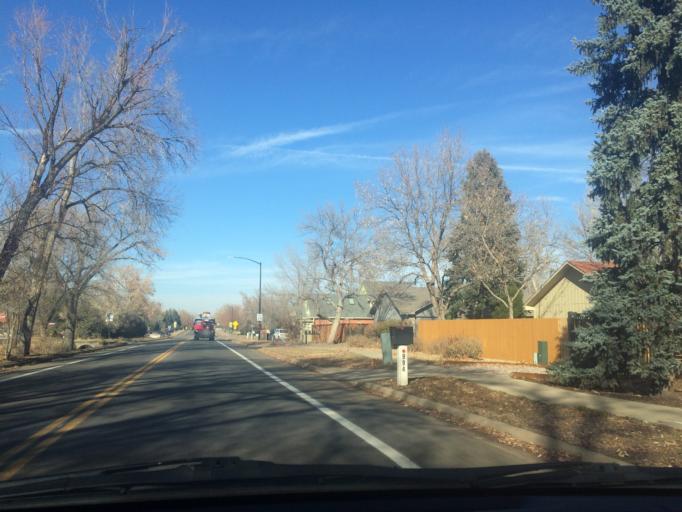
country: US
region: Colorado
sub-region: Boulder County
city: Boulder
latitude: 40.0049
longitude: -105.2253
